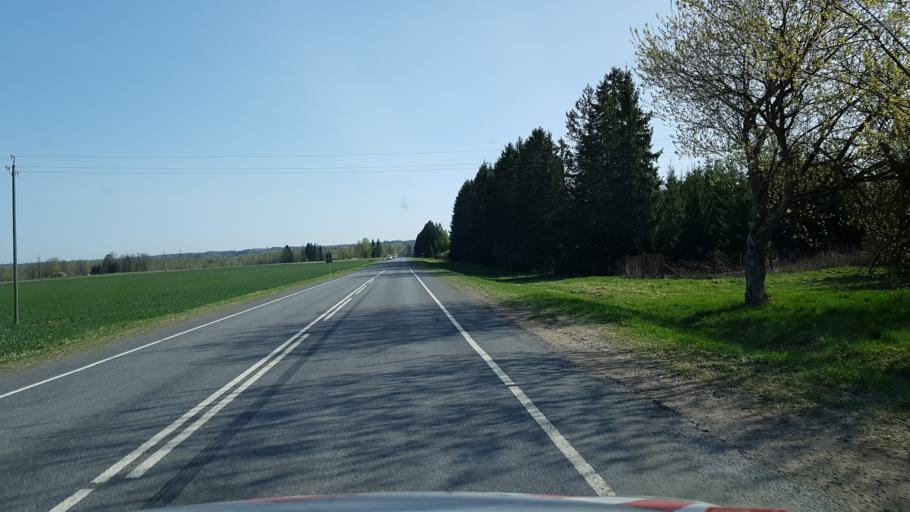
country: EE
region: Viljandimaa
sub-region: Karksi vald
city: Karksi-Nuia
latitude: 58.1852
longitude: 25.5111
